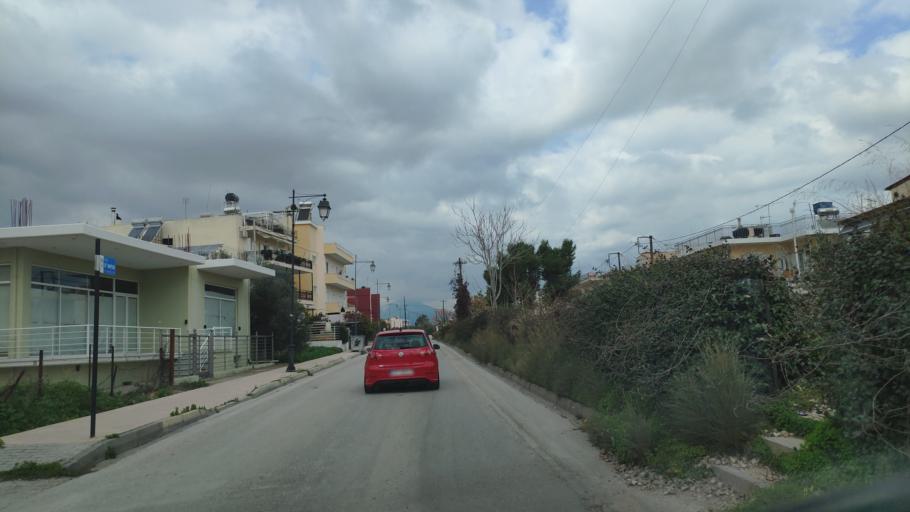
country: GR
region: Peloponnese
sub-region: Nomos Argolidos
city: Argos
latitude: 37.6414
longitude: 22.7323
